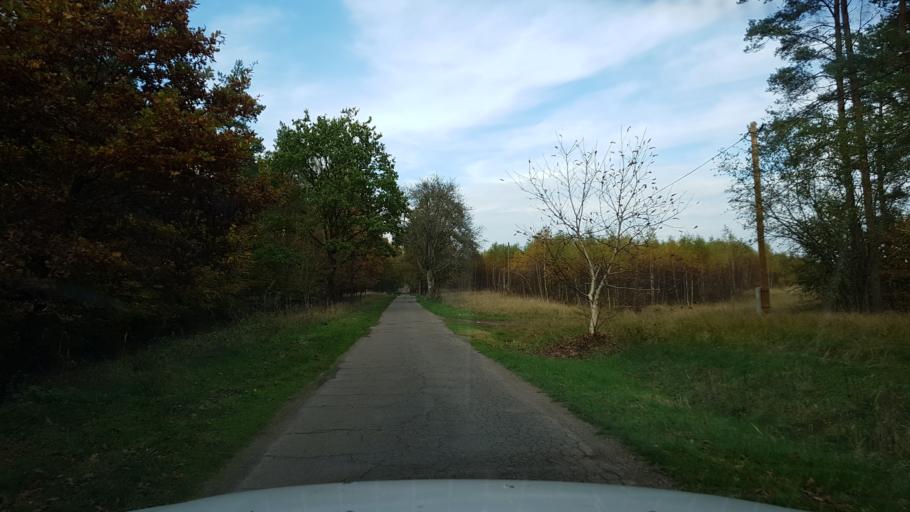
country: PL
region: West Pomeranian Voivodeship
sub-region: Powiat lobeski
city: Wegorzyno
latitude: 53.5100
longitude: 15.4958
